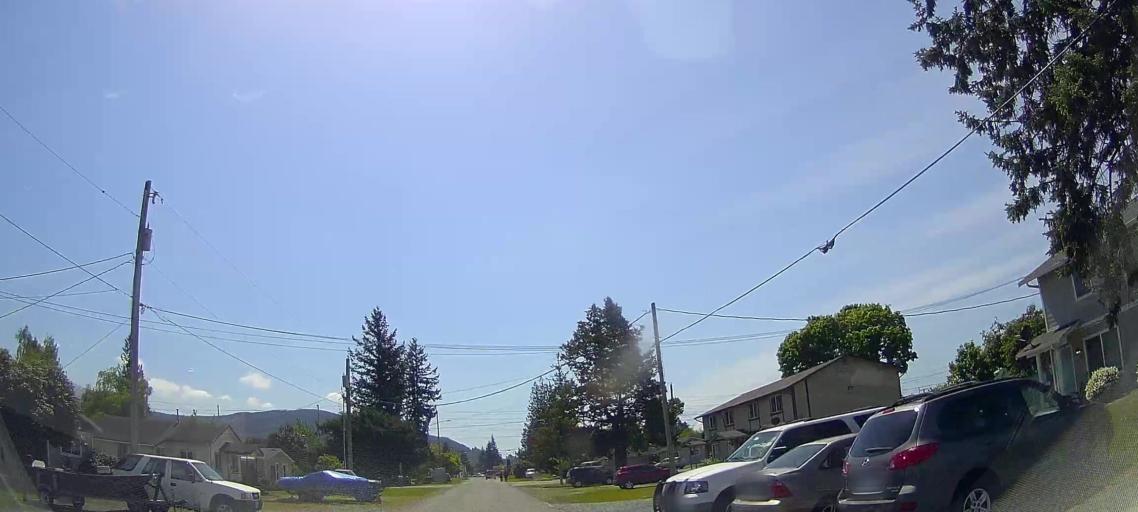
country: US
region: Washington
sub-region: Skagit County
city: Sedro-Woolley
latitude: 48.5082
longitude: -122.2367
